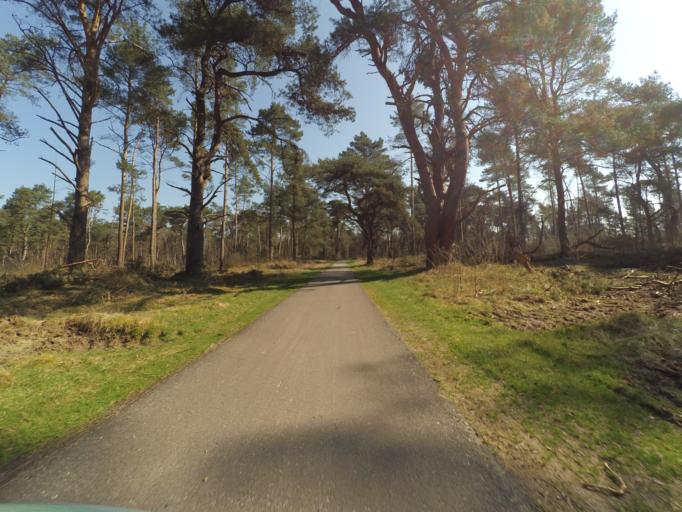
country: NL
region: Gelderland
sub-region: Gemeente Ede
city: Otterlo
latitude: 52.0700
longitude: 5.8472
